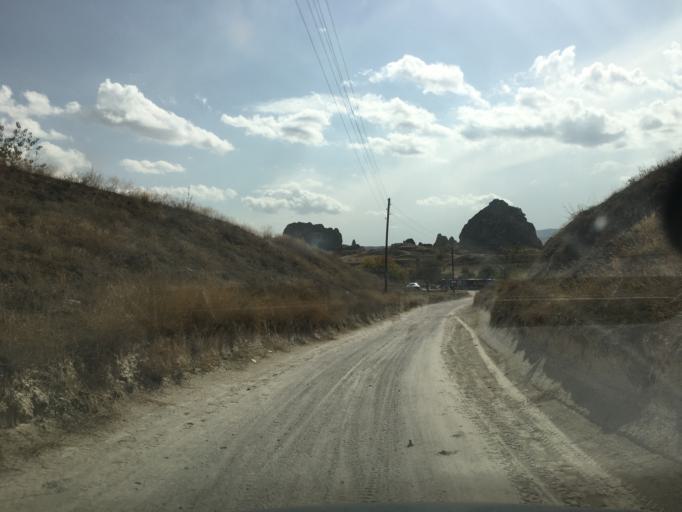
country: TR
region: Nevsehir
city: Goereme
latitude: 38.6636
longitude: 34.8413
